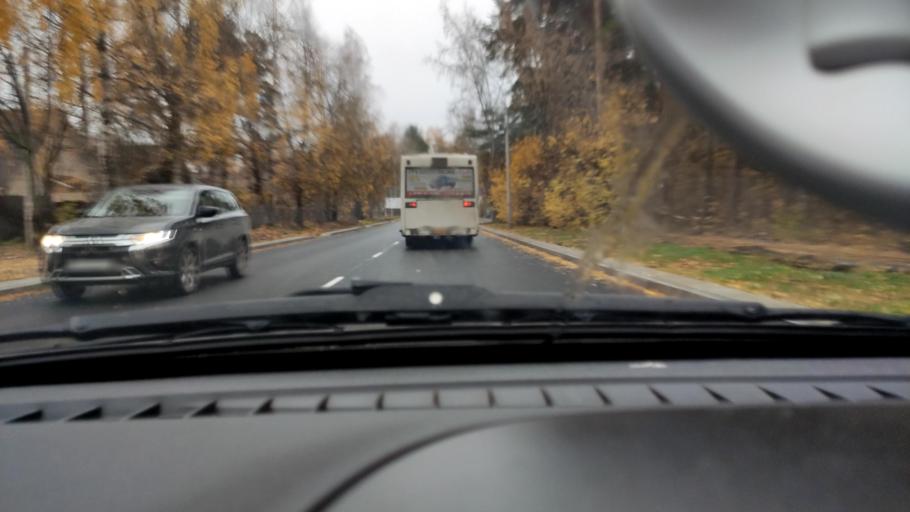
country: RU
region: Perm
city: Kondratovo
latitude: 58.0226
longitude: 56.0129
